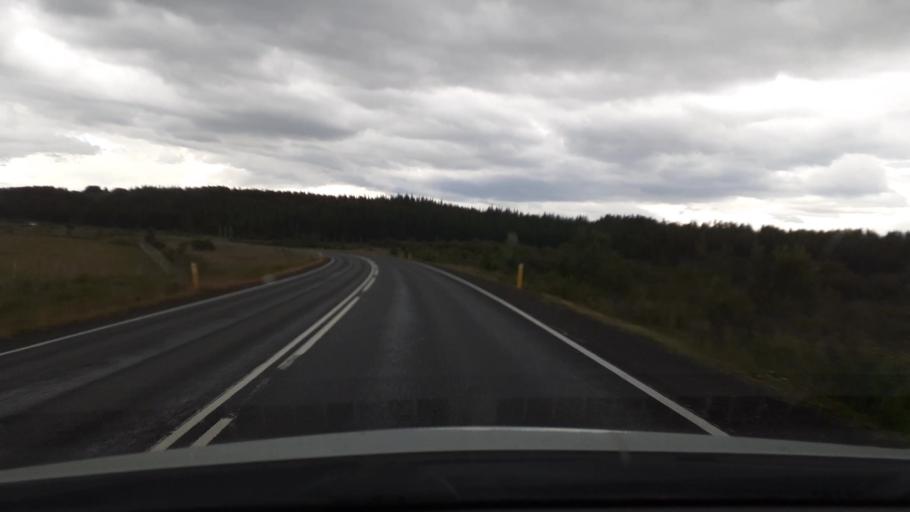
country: IS
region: West
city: Borgarnes
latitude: 64.6576
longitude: -21.7181
